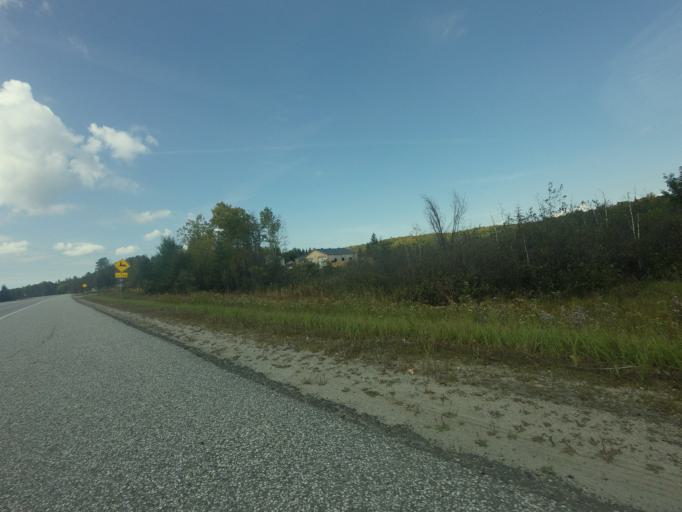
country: CA
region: Quebec
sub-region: Laurentides
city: Mont-Laurier
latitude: 46.5598
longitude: -75.6262
